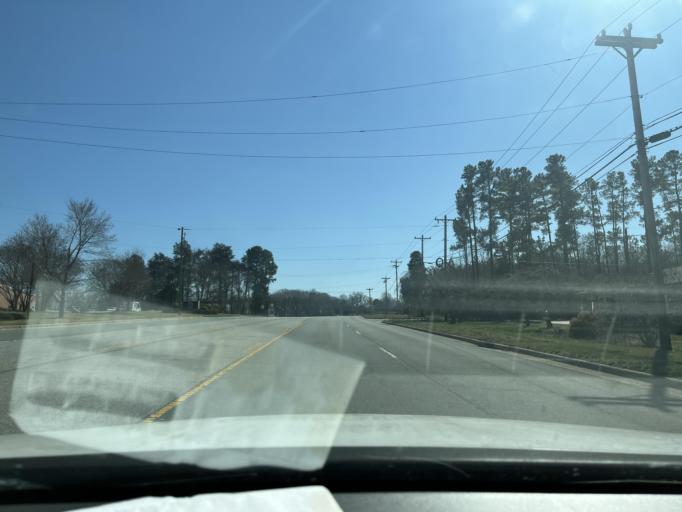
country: US
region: North Carolina
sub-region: Guilford County
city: Jamestown
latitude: 35.9841
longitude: -79.9028
